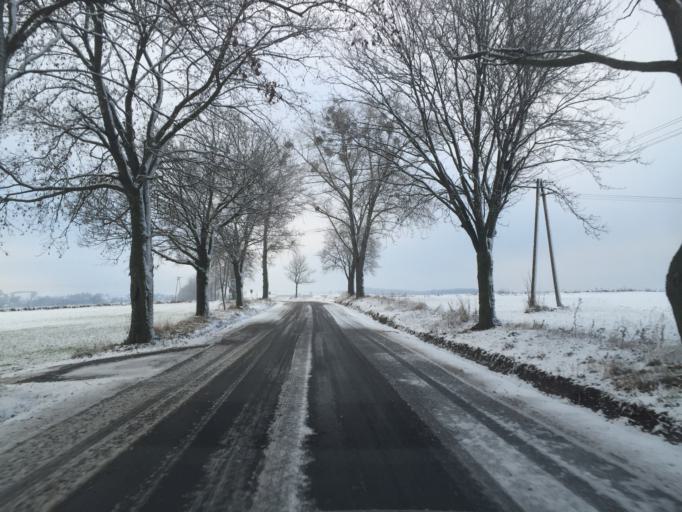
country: PL
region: Kujawsko-Pomorskie
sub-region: Powiat brodnicki
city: Bartniczka
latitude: 53.2527
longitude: 19.6583
